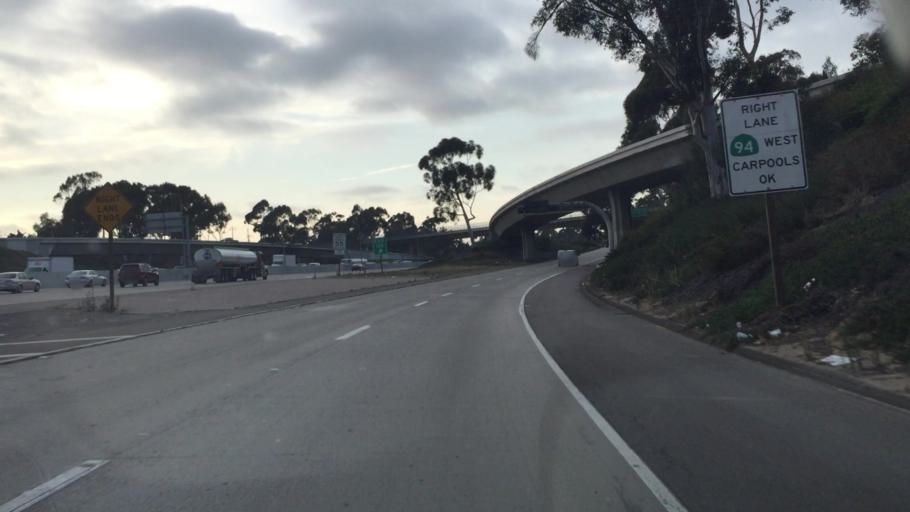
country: US
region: California
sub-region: San Diego County
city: National City
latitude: 32.7124
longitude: -117.1011
